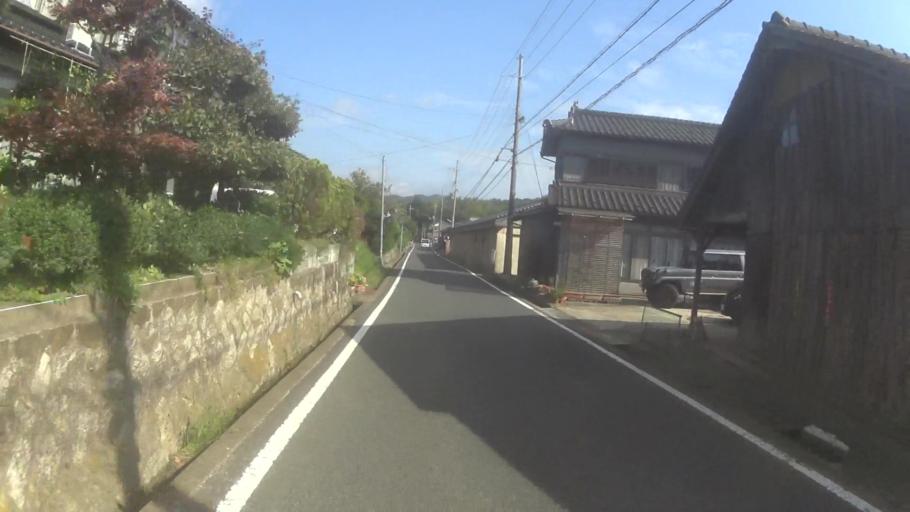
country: JP
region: Kyoto
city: Miyazu
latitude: 35.7082
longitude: 135.0876
